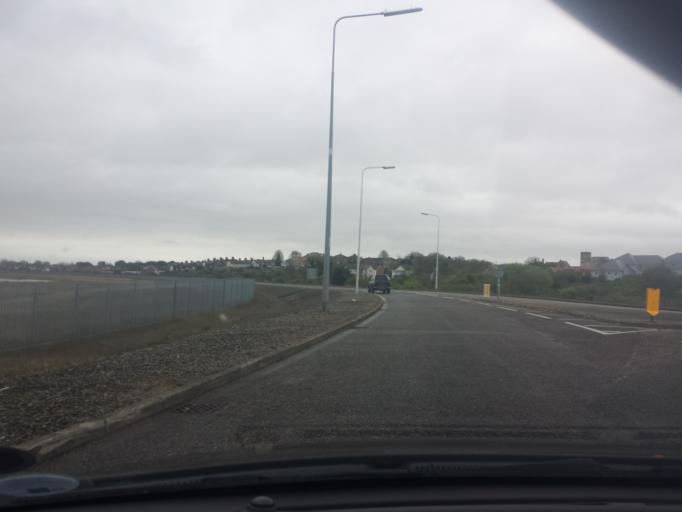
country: GB
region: England
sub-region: Essex
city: Dovercourt
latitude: 51.9396
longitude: 1.2716
